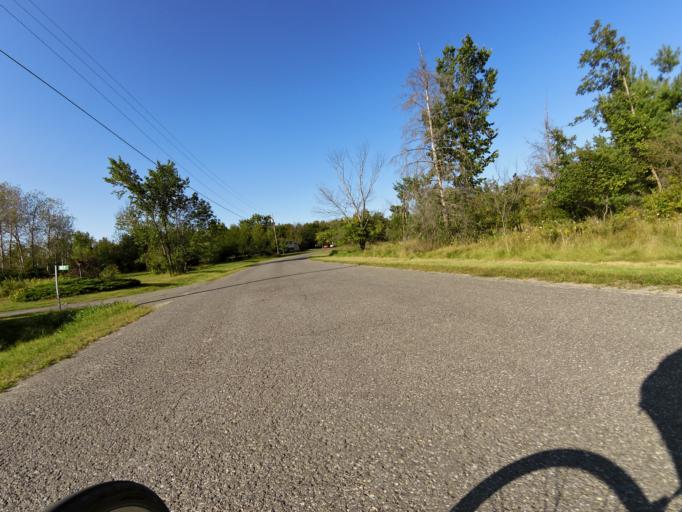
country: CA
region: Ontario
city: Bells Corners
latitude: 45.4791
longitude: -76.0387
